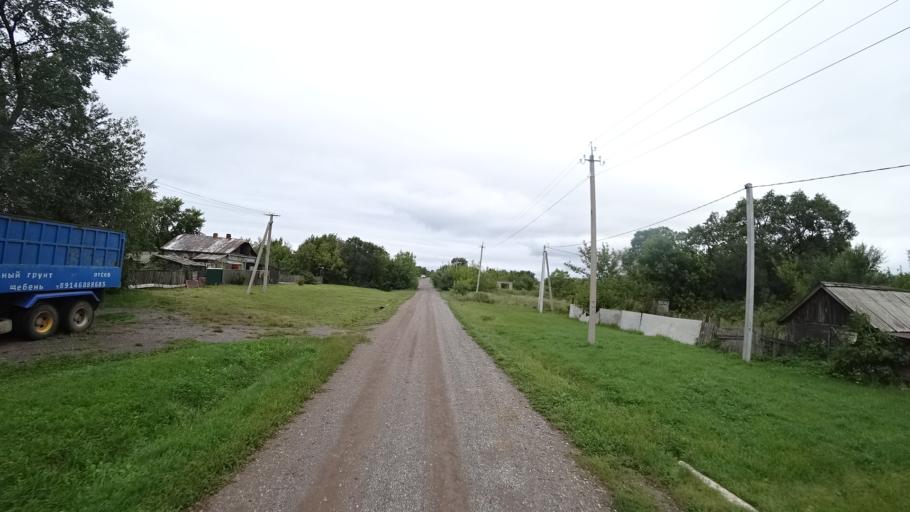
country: RU
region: Primorskiy
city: Chernigovka
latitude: 44.3327
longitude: 132.5996
